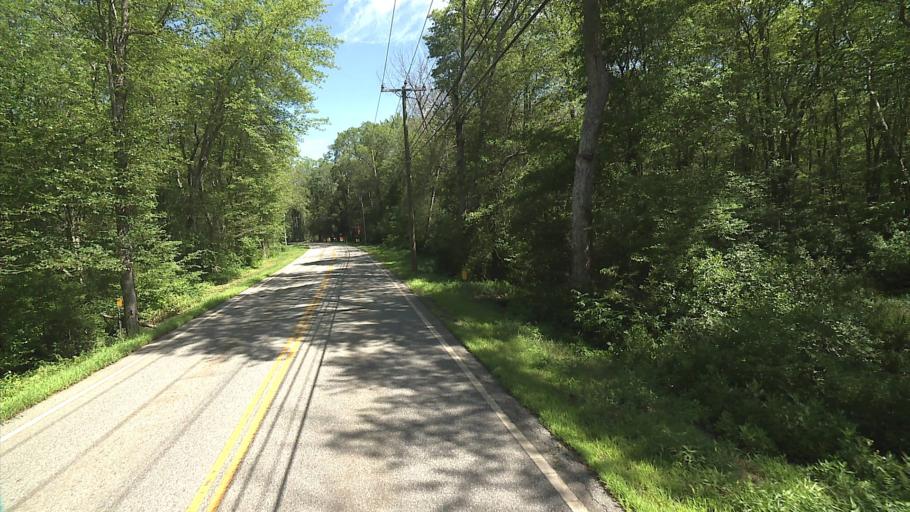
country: US
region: Connecticut
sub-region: Windham County
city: Windham
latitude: 41.7565
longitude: -72.0606
